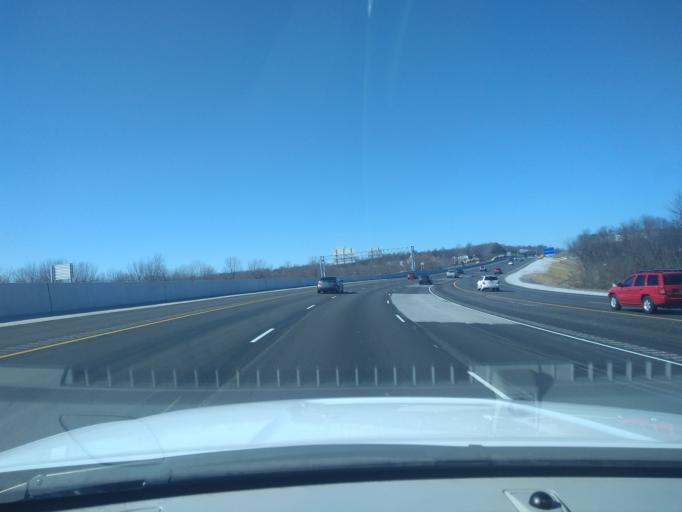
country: US
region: Arkansas
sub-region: Washington County
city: Johnson
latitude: 36.1140
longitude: -94.1745
